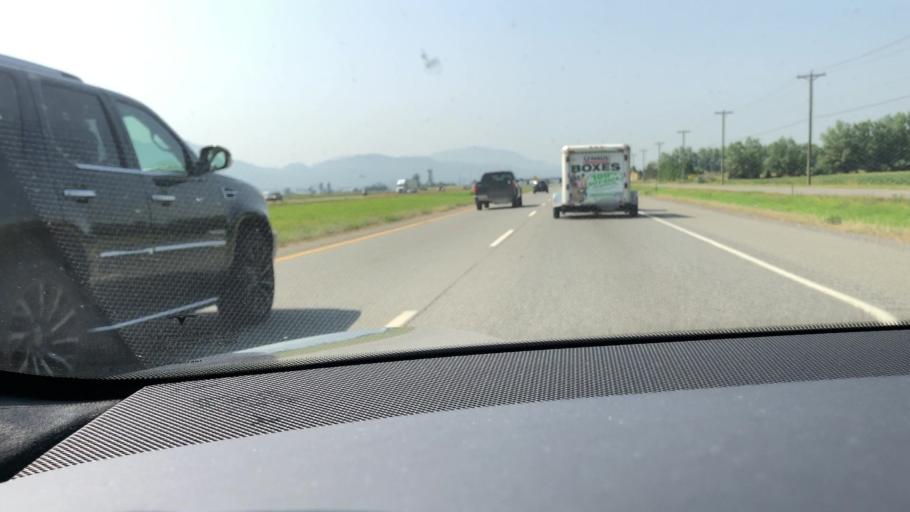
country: CA
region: British Columbia
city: Abbotsford
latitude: 49.0960
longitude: -122.1208
